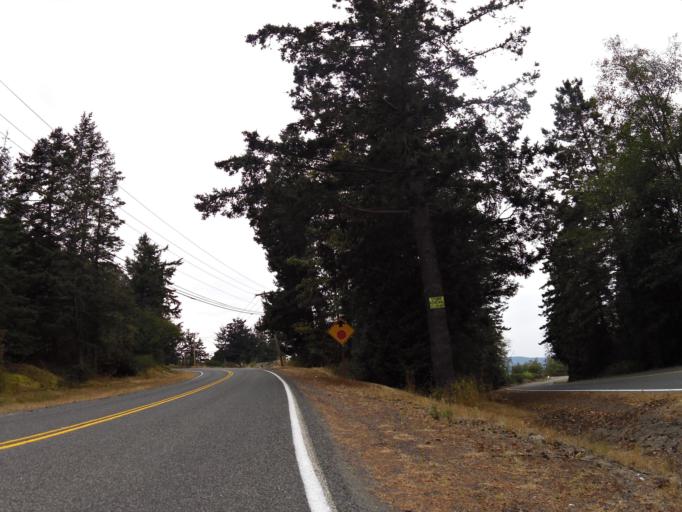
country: US
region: Washington
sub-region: Skagit County
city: Anacortes
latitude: 48.4524
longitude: -122.6504
